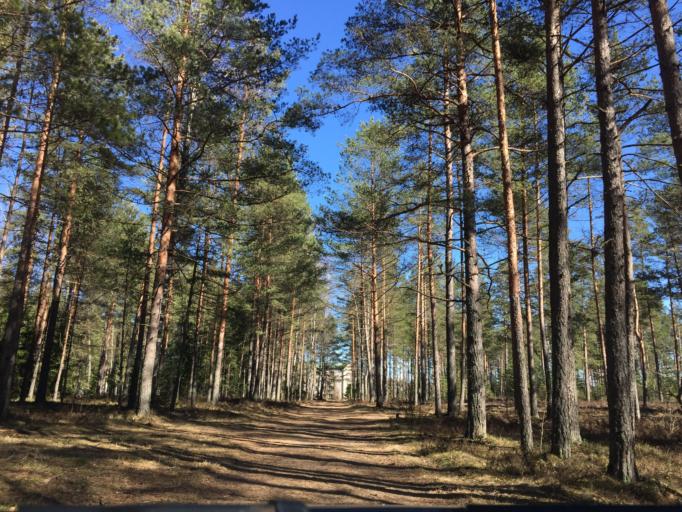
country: LV
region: Incukalns
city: Vangazi
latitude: 57.0926
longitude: 24.5359
